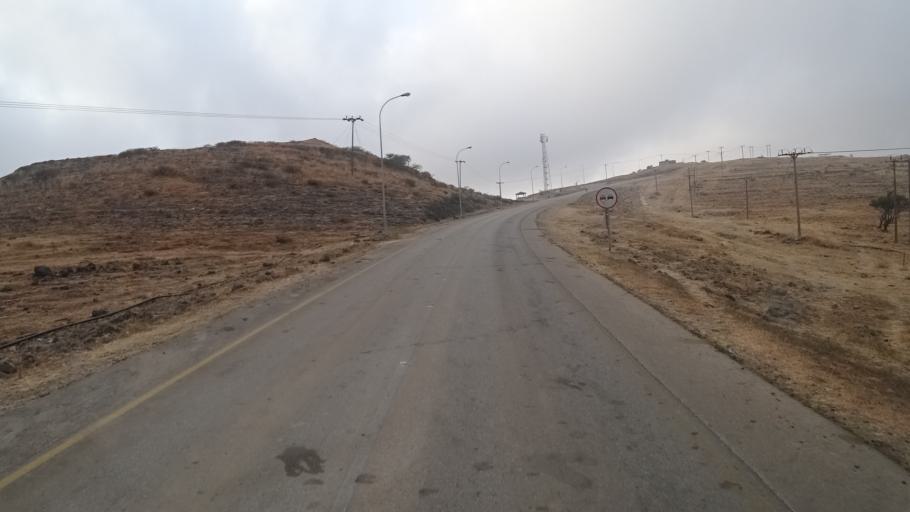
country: OM
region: Zufar
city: Salalah
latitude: 17.1204
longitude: 53.9776
